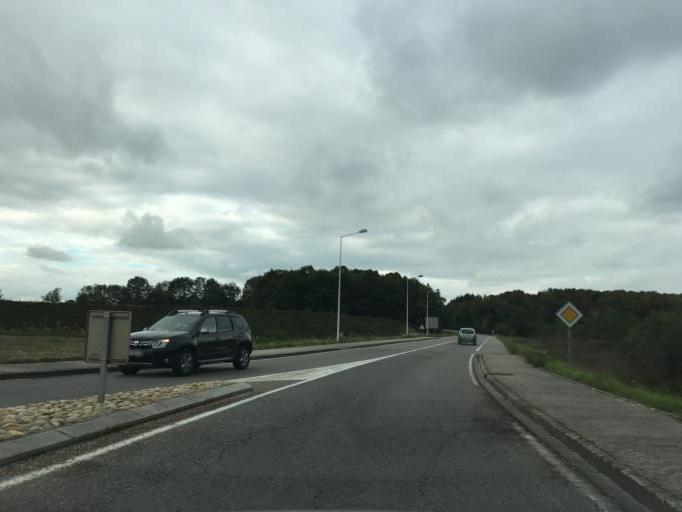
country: FR
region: Rhone-Alpes
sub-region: Departement de l'Ain
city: Montagnat
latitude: 46.2119
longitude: 5.2721
